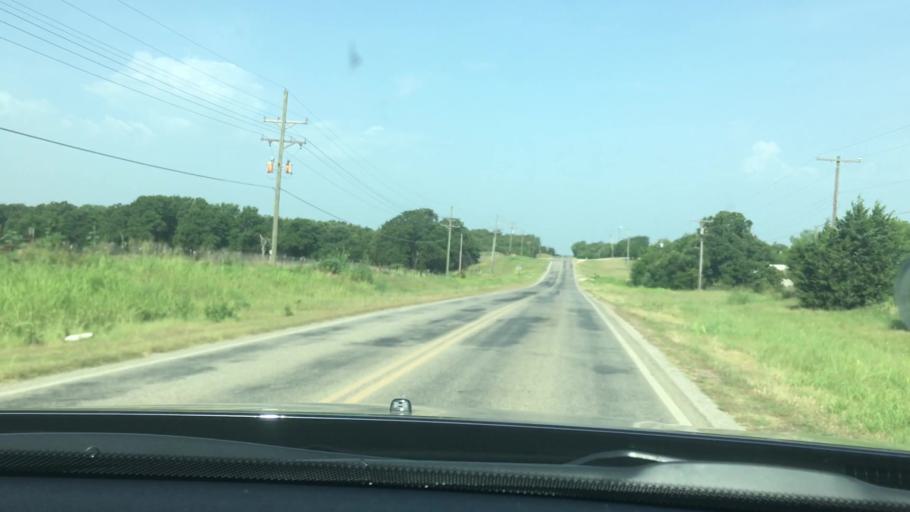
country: US
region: Oklahoma
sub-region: Pontotoc County
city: Byng
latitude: 34.8649
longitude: -96.6024
